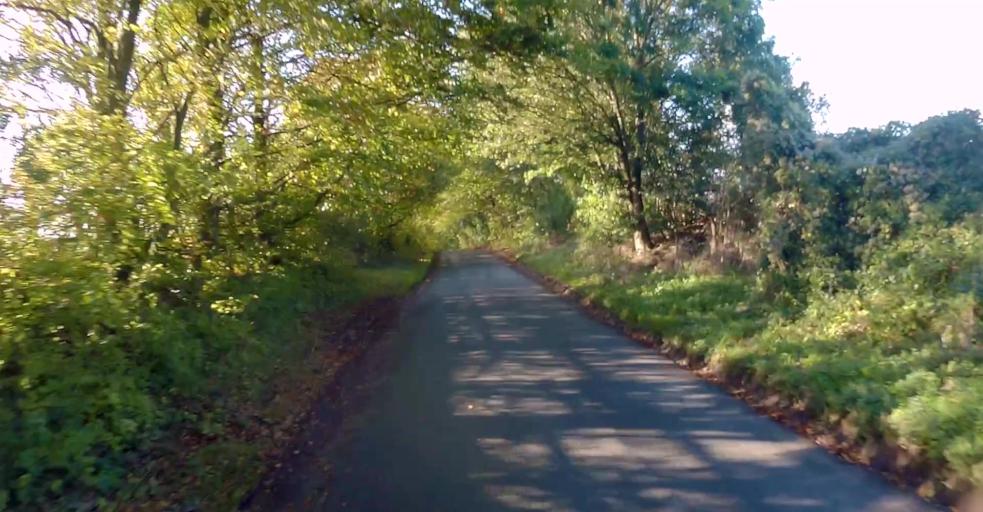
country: GB
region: England
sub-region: Hampshire
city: Long Sutton
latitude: 51.2145
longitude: -0.9171
